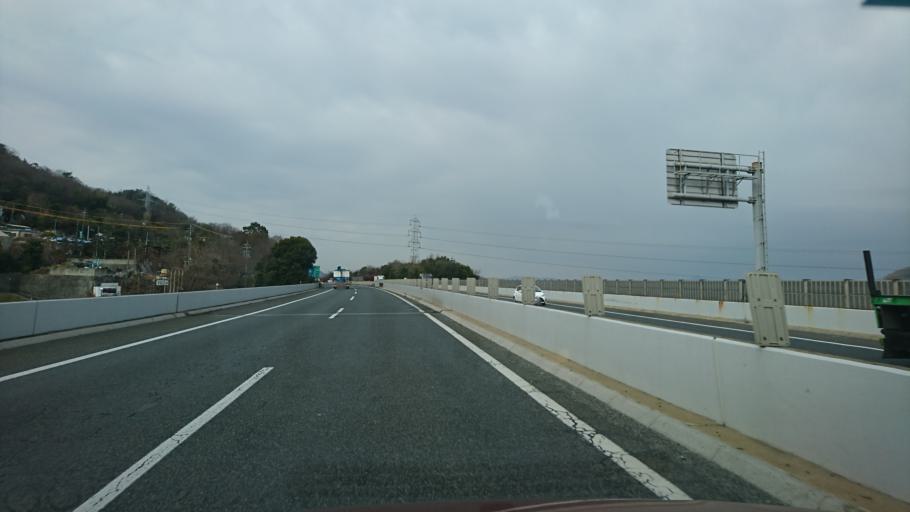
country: JP
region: Hiroshima
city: Fukuyama
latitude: 34.5161
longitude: 133.3879
